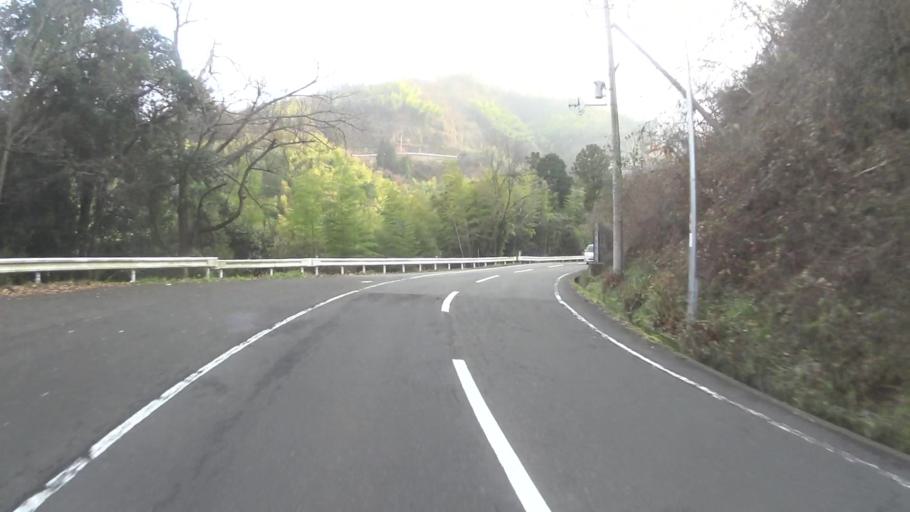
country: JP
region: Kyoto
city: Maizuru
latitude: 35.4423
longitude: 135.3946
